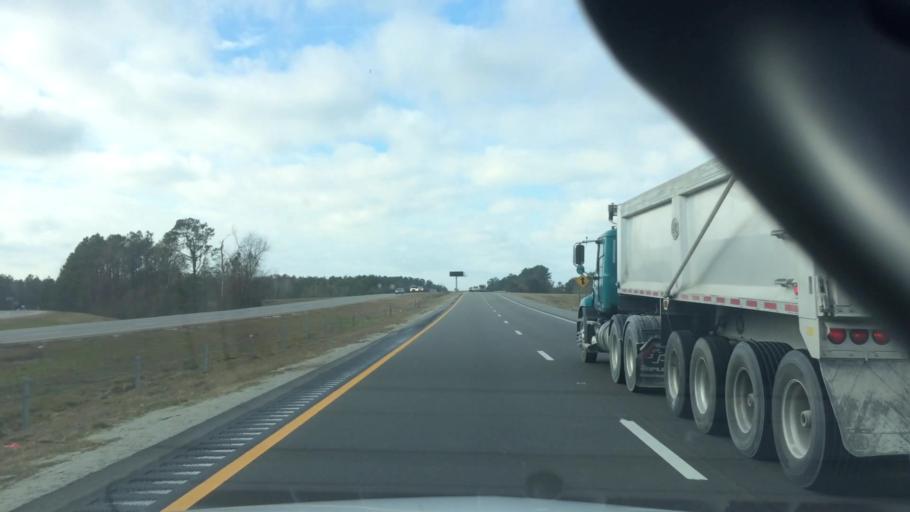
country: US
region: North Carolina
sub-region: New Hanover County
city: Wrightsboro
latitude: 34.3163
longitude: -77.9178
